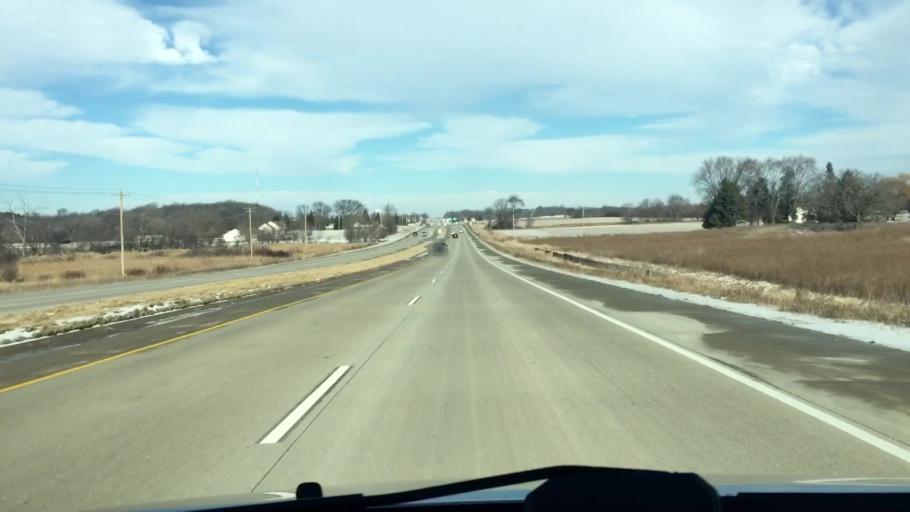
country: US
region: Wisconsin
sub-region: Waukesha County
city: Mukwonago
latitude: 42.9126
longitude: -88.3454
